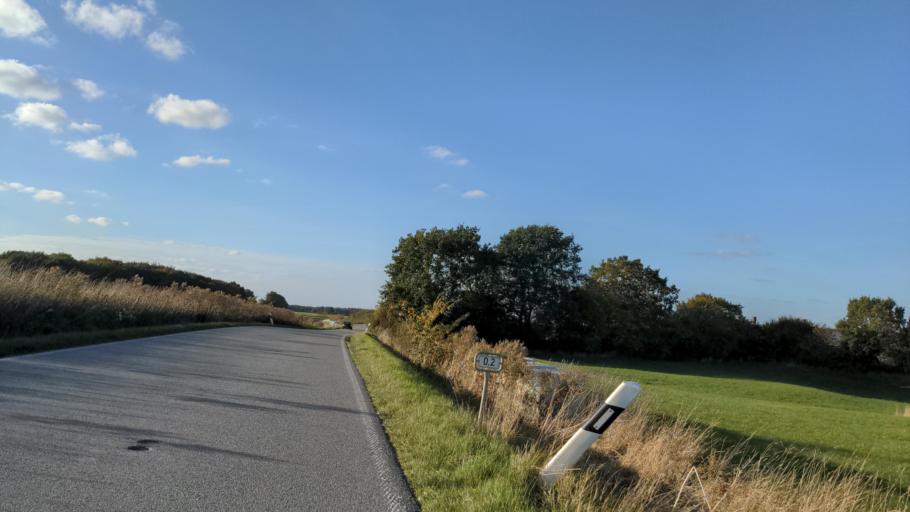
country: DE
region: Schleswig-Holstein
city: Pronstorf
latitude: 53.9591
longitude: 10.5226
